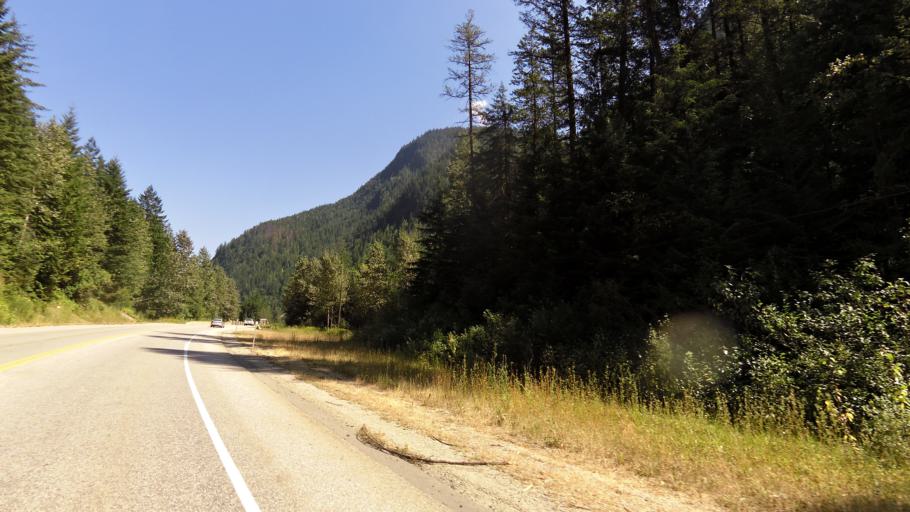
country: CA
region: British Columbia
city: Revelstoke
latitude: 50.9629
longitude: -118.3839
